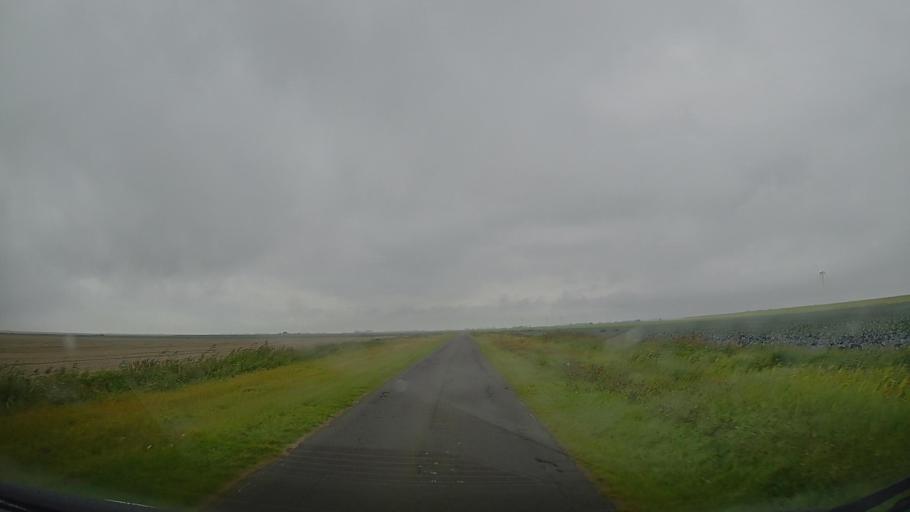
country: DE
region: Schleswig-Holstein
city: Friedrichsgabekoog
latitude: 54.1075
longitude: 8.9861
